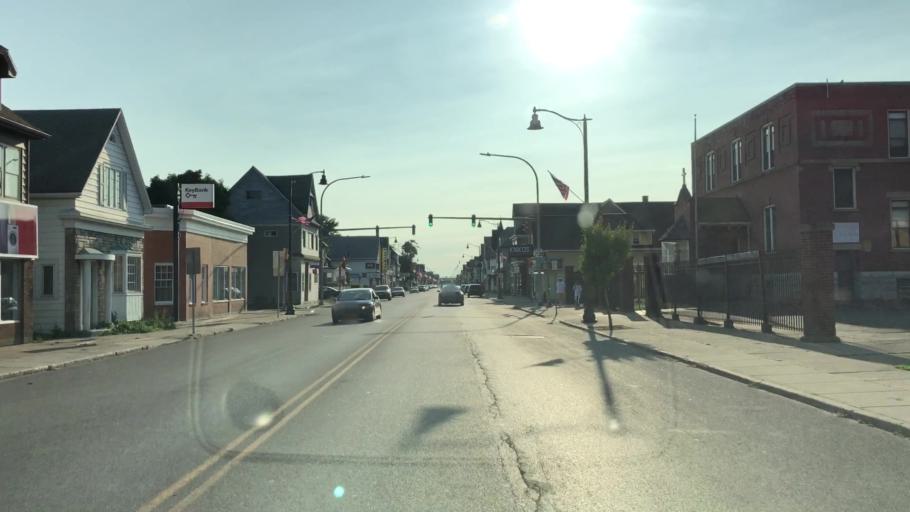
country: US
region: New York
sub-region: Erie County
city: West Seneca
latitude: 42.8718
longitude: -78.8024
